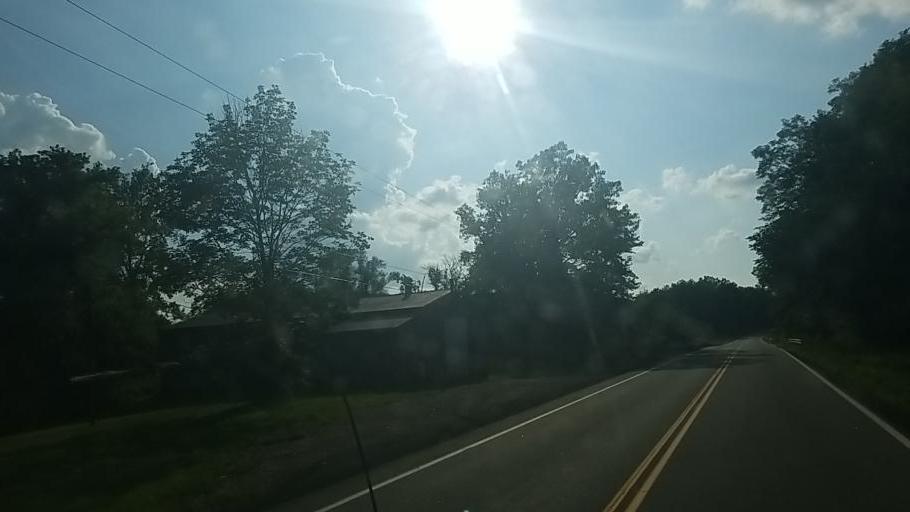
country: US
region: Ohio
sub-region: Wayne County
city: West Salem
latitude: 40.8954
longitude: -82.1500
